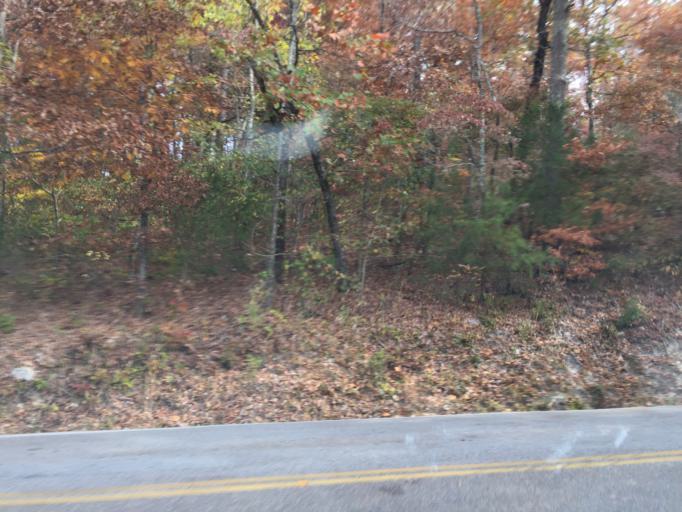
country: US
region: Tennessee
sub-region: Hamilton County
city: Harrison
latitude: 35.1129
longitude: -85.0821
